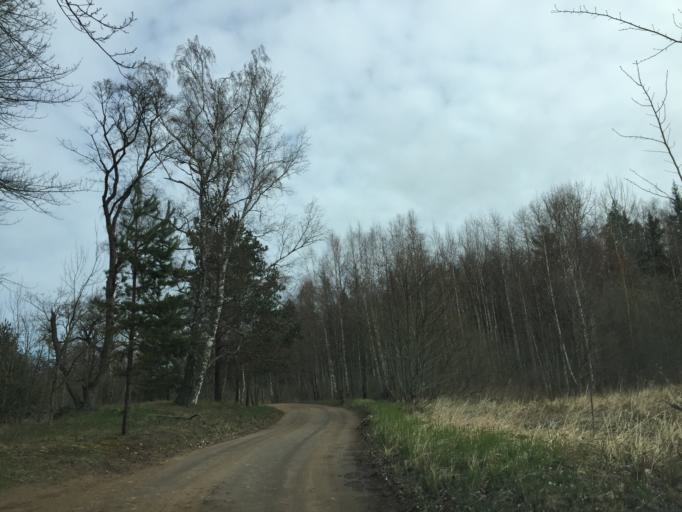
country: LV
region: Salacgrivas
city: Salacgriva
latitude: 57.5182
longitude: 24.3792
